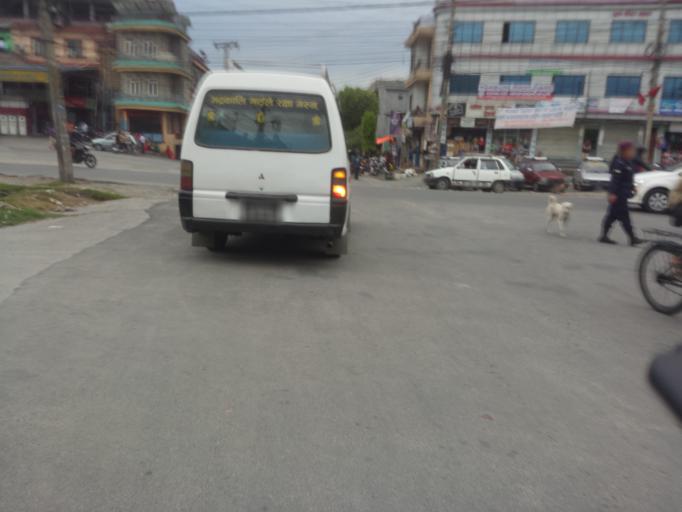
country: NP
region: Western Region
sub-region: Gandaki Zone
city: Pokhara
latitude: 28.2064
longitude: 83.9947
